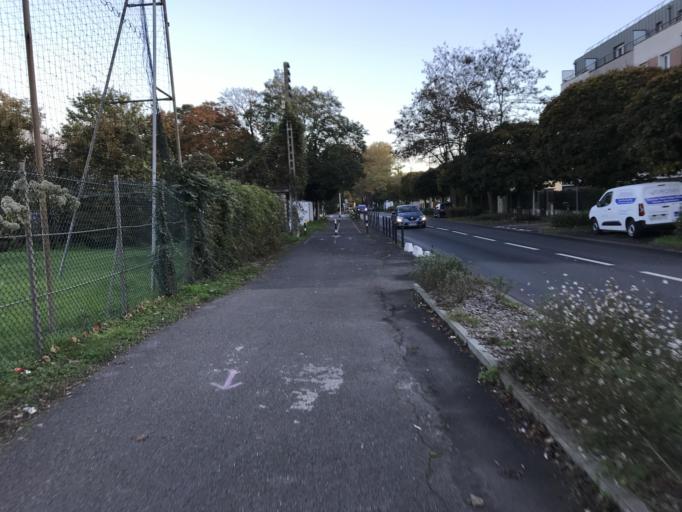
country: FR
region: Ile-de-France
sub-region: Departement de l'Essonne
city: Athis-Mons
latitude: 48.7115
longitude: 2.3818
